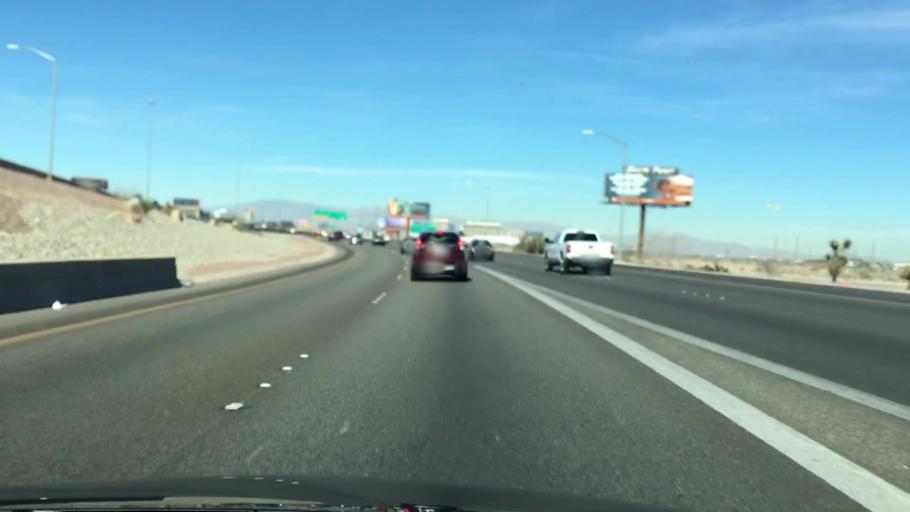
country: US
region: Nevada
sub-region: Clark County
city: Paradise
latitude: 36.0460
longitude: -115.1801
